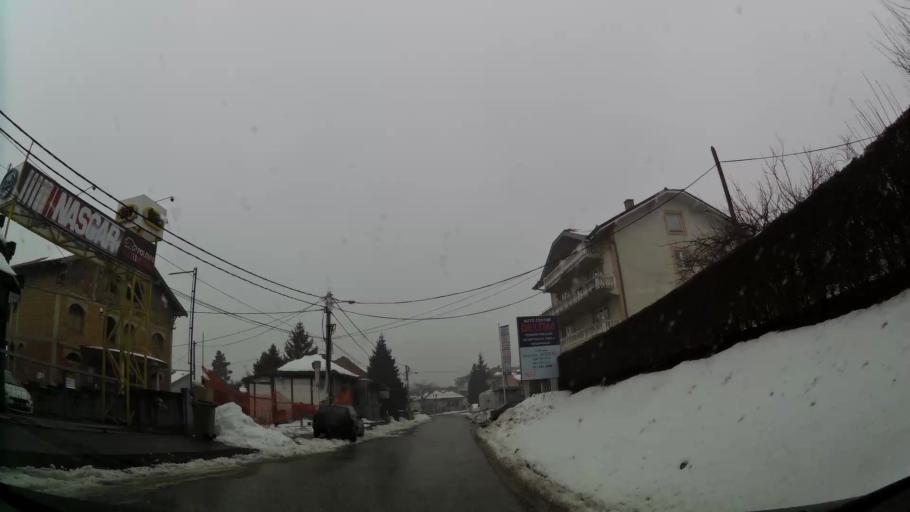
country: RS
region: Central Serbia
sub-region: Belgrade
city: Zvezdara
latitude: 44.7765
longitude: 20.5302
